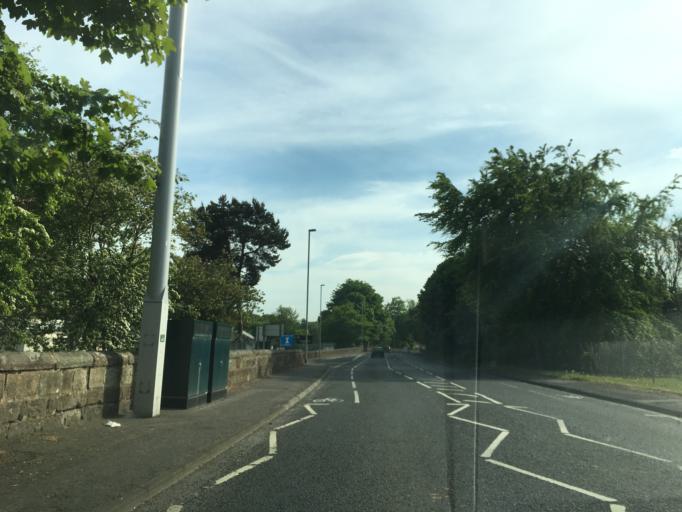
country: GB
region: Scotland
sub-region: Midlothian
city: Penicuik
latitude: 55.8452
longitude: -3.2048
